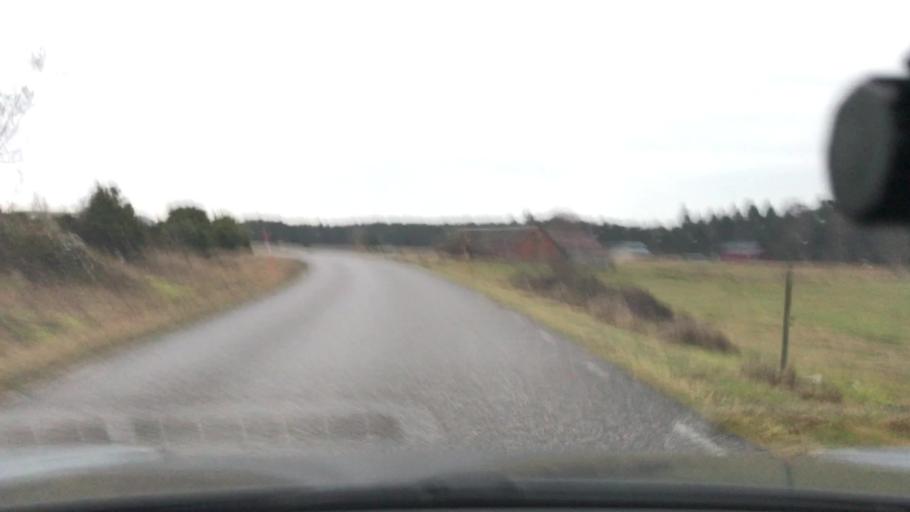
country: SE
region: Gotland
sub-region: Gotland
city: Slite
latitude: 57.3977
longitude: 18.8058
